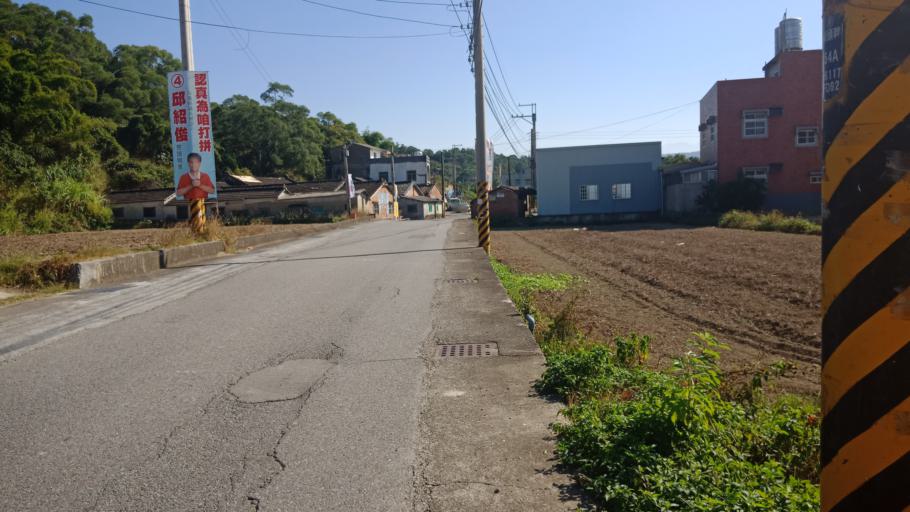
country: TW
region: Taiwan
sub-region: Miaoli
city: Miaoli
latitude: 24.4837
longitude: 120.7062
